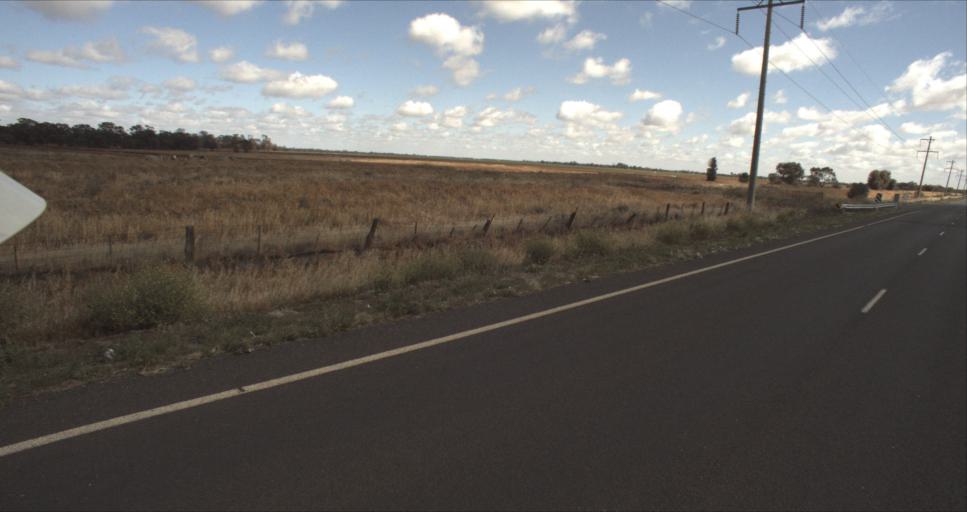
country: AU
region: New South Wales
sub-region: Murrumbidgee Shire
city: Darlington Point
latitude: -34.5420
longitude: 146.1720
